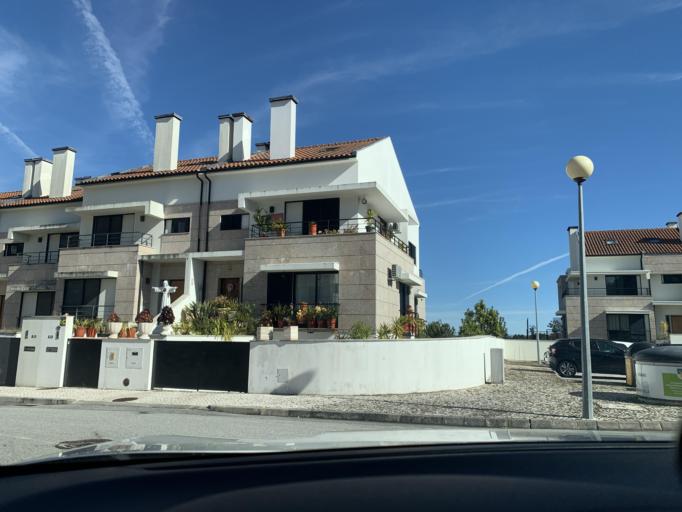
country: PT
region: Viseu
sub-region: Viseu
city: Viseu
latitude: 40.6355
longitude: -7.9274
